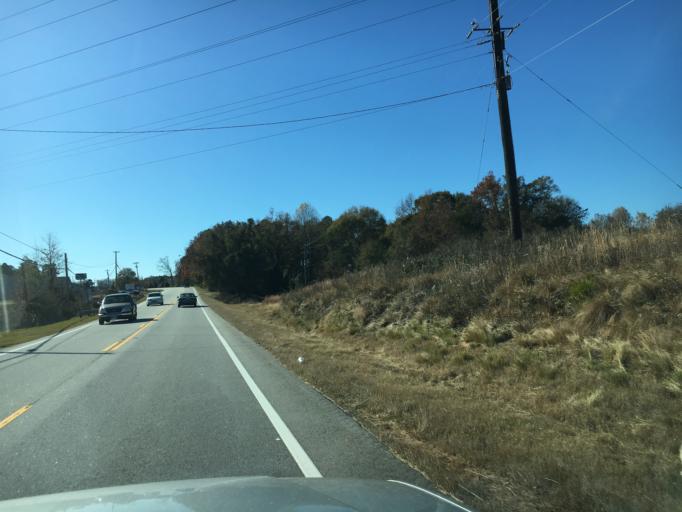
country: US
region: Georgia
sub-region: Hart County
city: Hartwell
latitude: 34.3399
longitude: -82.9535
